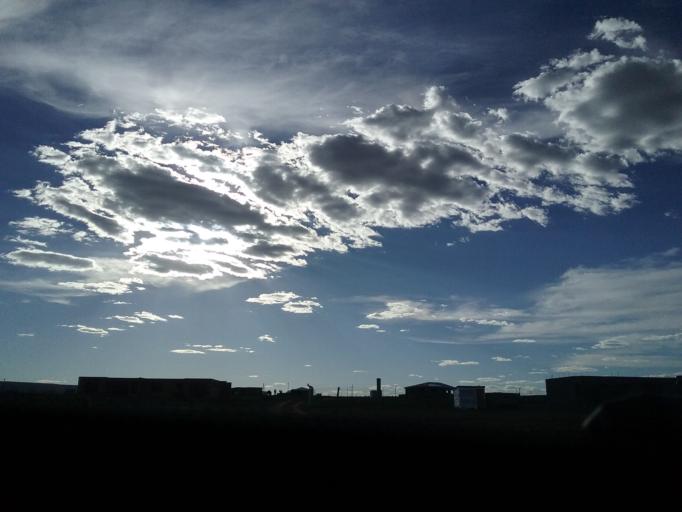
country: LS
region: Maseru
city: Maseru
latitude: -29.4270
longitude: 27.5732
